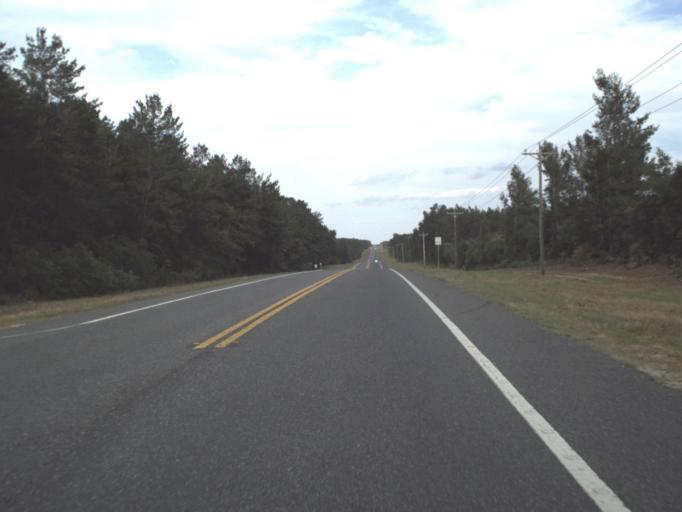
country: US
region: Florida
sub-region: Lake County
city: Astor
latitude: 29.1773
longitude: -81.7696
